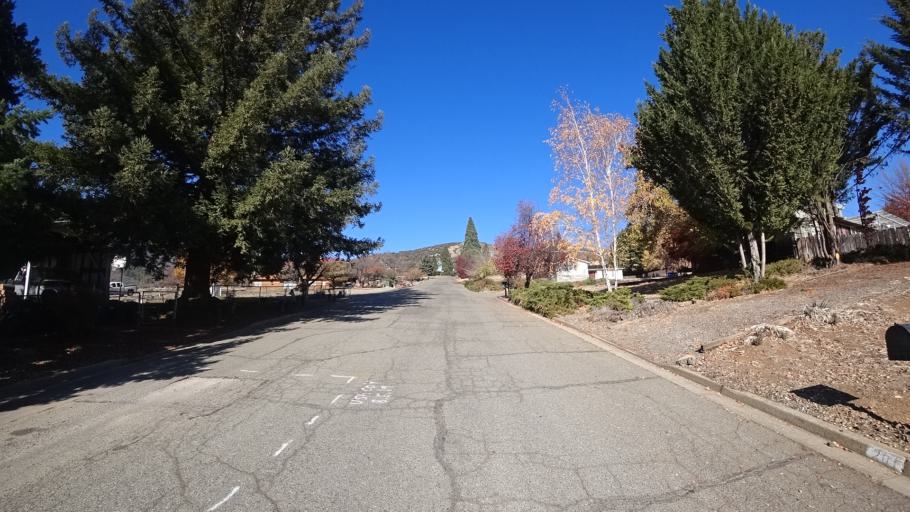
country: US
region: California
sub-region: Siskiyou County
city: Yreka
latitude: 41.7392
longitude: -122.6586
